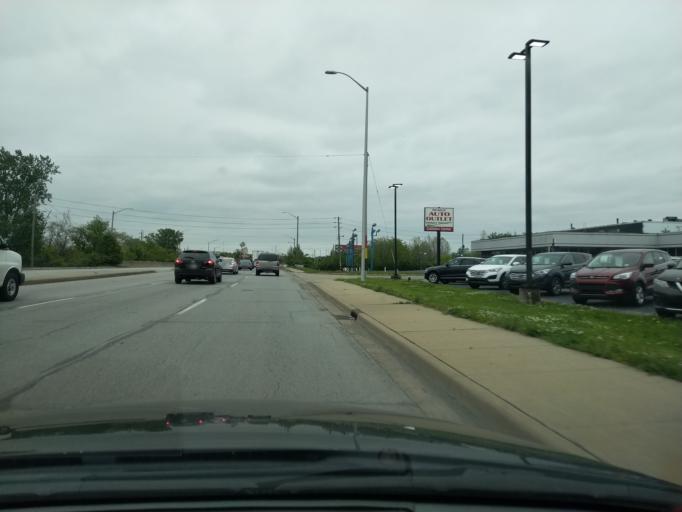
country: US
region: Indiana
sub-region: Marion County
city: Speedway
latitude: 39.8239
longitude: -86.2335
